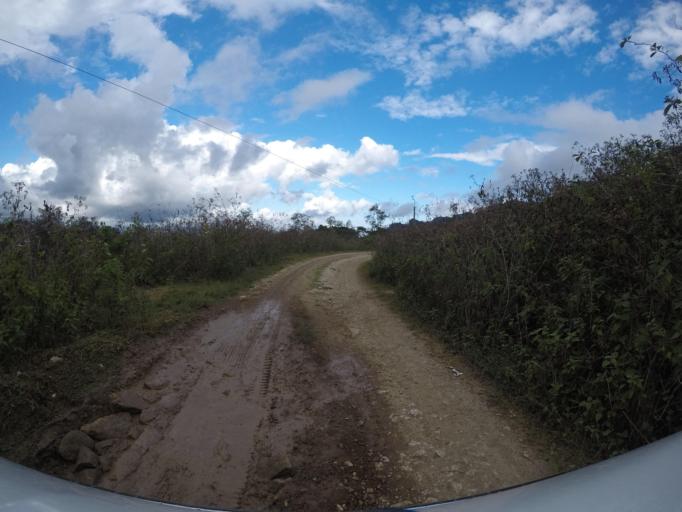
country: TL
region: Baucau
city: Venilale
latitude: -8.6788
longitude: 126.6367
